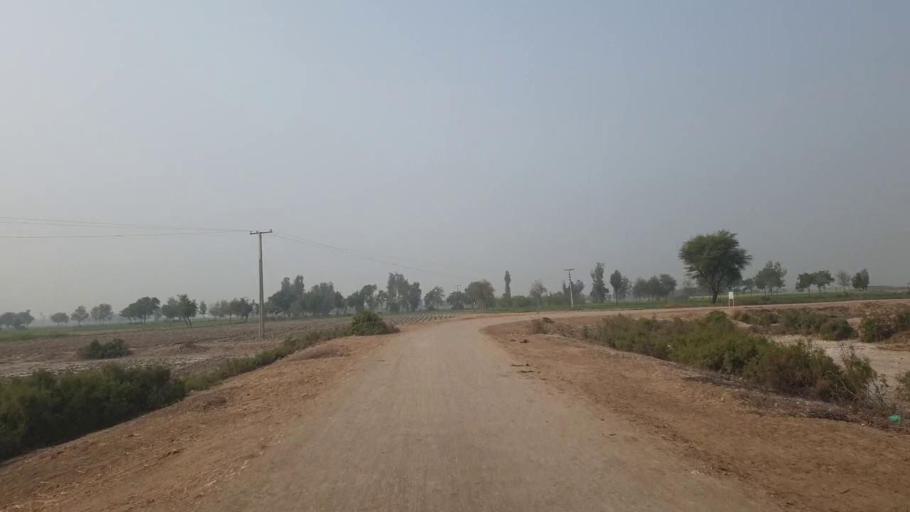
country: PK
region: Sindh
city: Bhit Shah
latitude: 25.8408
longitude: 68.5781
